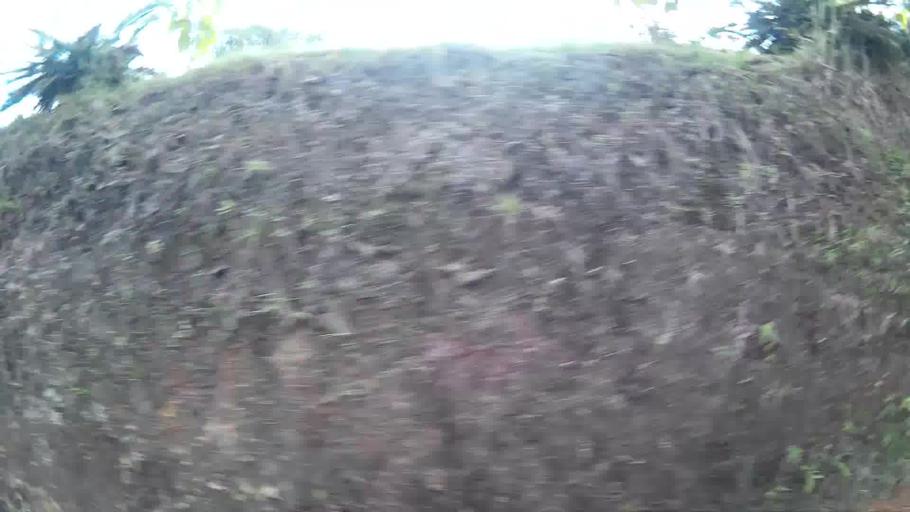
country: CO
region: Valle del Cauca
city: Ulloa
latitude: 4.7318
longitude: -75.7152
